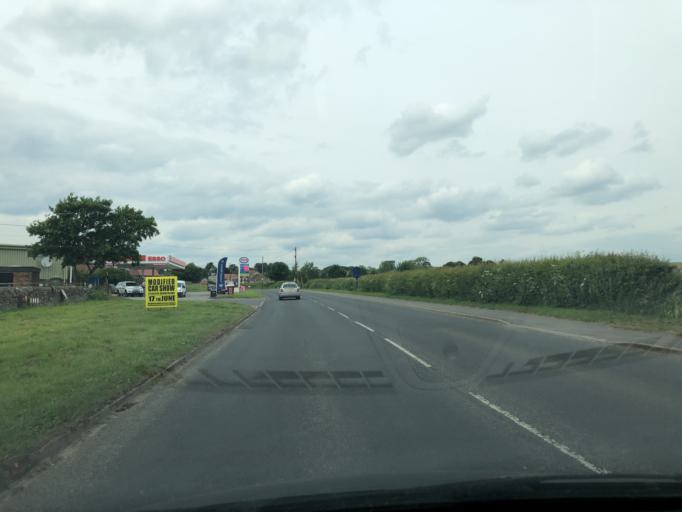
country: GB
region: England
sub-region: North Yorkshire
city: Pickering
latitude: 54.2542
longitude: -0.7951
